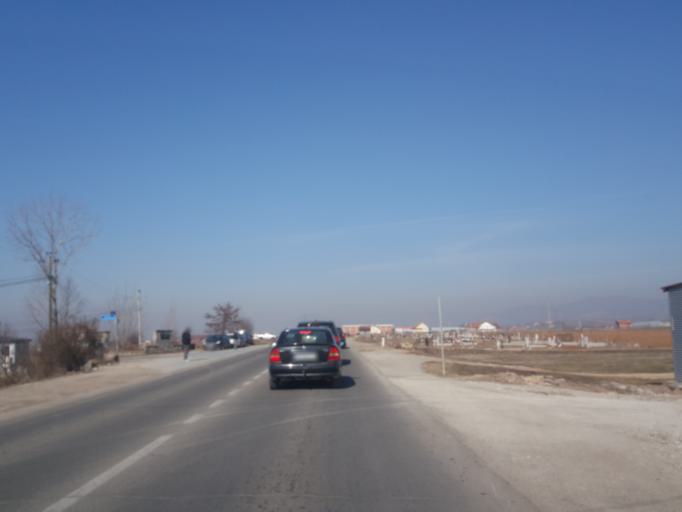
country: XK
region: Mitrovica
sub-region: Vushtrri
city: Vushtrri
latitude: 42.7867
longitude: 21.0081
